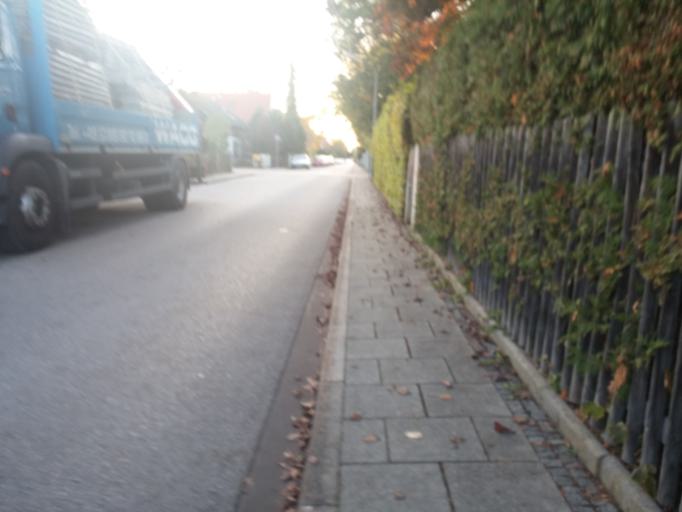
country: DE
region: Bavaria
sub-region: Upper Bavaria
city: Haar
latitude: 48.1051
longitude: 11.7464
